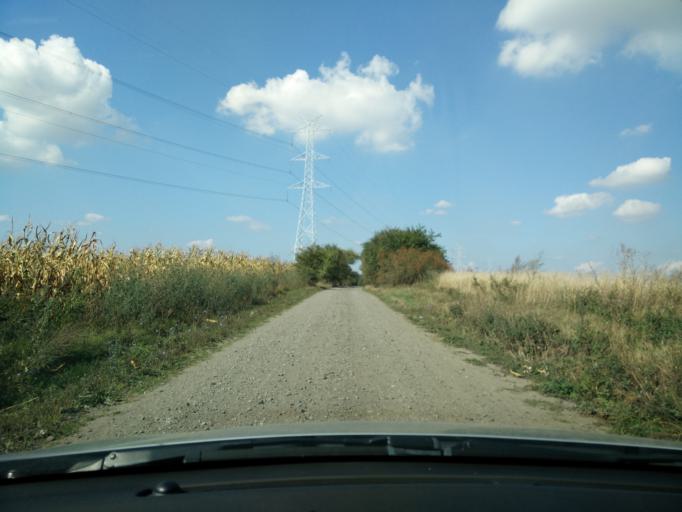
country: PL
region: Greater Poland Voivodeship
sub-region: Powiat poznanski
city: Kleszczewo
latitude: 52.2559
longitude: 17.1981
